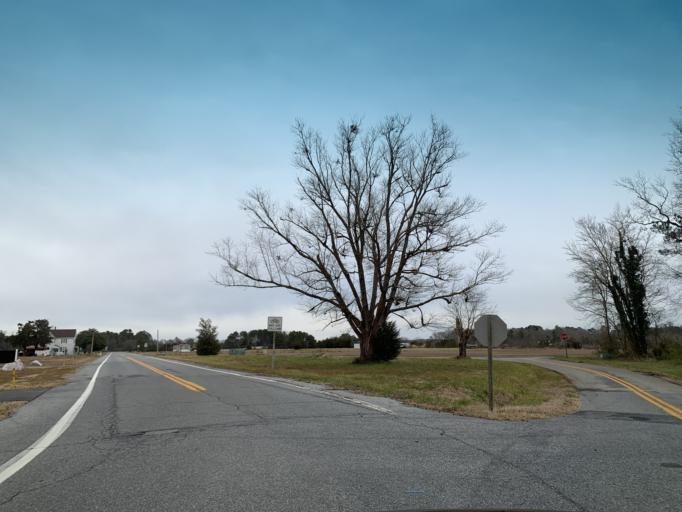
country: US
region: Maryland
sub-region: Worcester County
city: Pocomoke City
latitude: 38.0195
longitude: -75.6101
